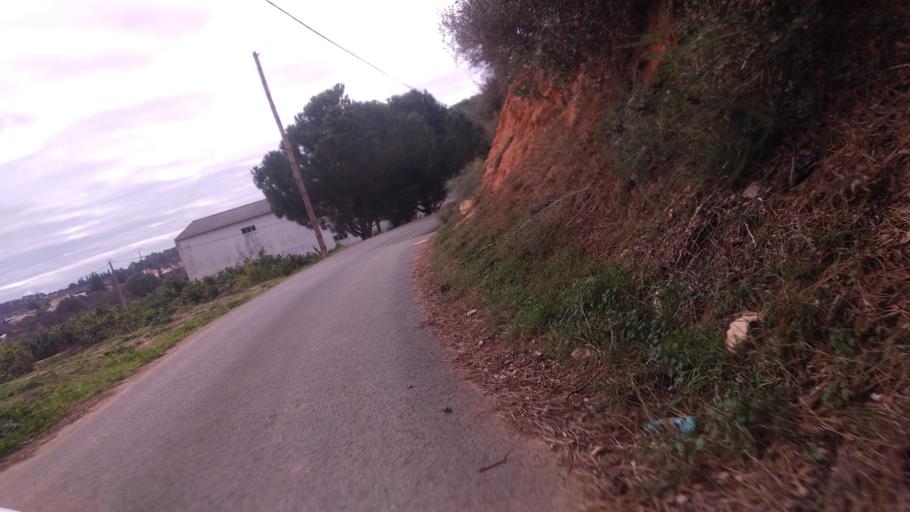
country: PT
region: Faro
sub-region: Faro
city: Santa Barbara de Nexe
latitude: 37.0697
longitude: -7.9715
